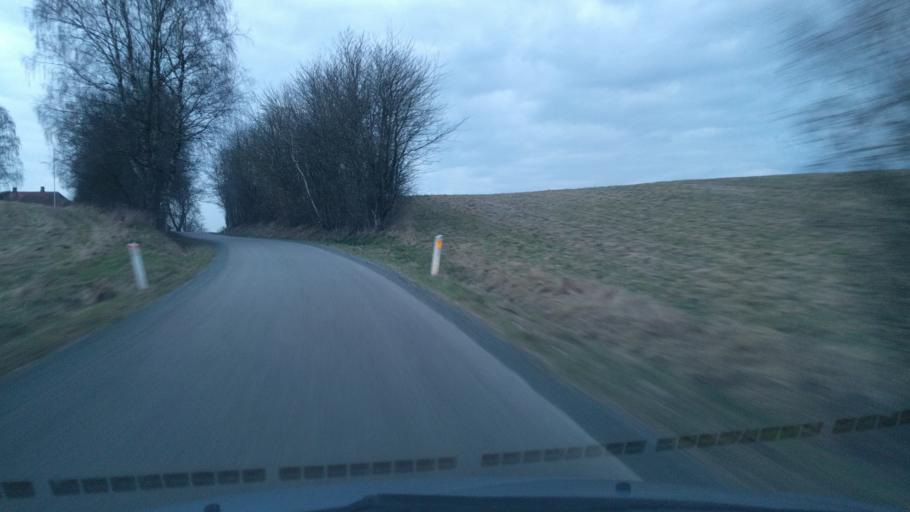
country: DK
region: South Denmark
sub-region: Haderslev Kommune
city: Haderslev
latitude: 55.2586
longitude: 9.4265
